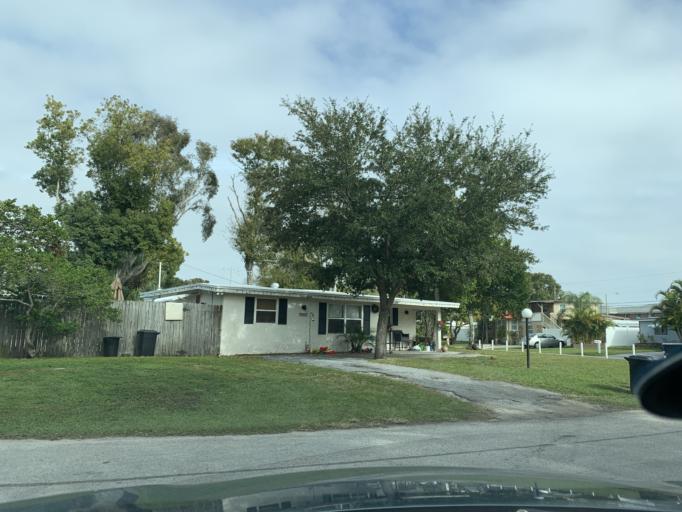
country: US
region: Florida
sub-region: Pinellas County
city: Ridgecrest
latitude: 27.8819
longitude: -82.7816
